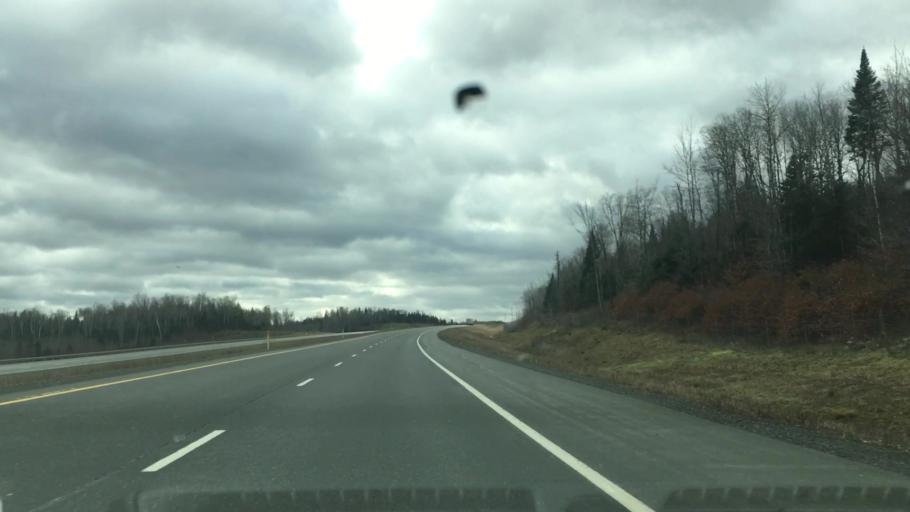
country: US
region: Maine
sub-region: Aroostook County
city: Fort Fairfield
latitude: 46.6660
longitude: -67.7302
